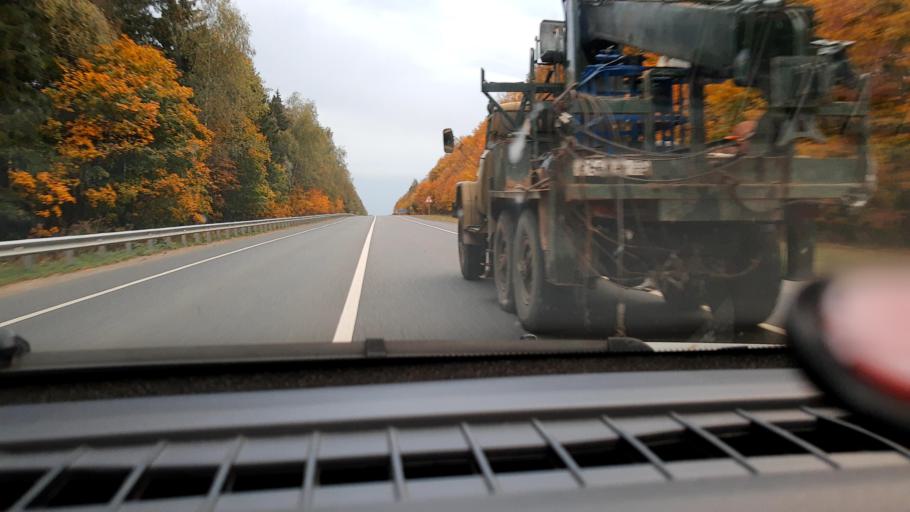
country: RU
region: Vladimir
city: Orgtrud
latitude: 56.1998
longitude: 40.8192
